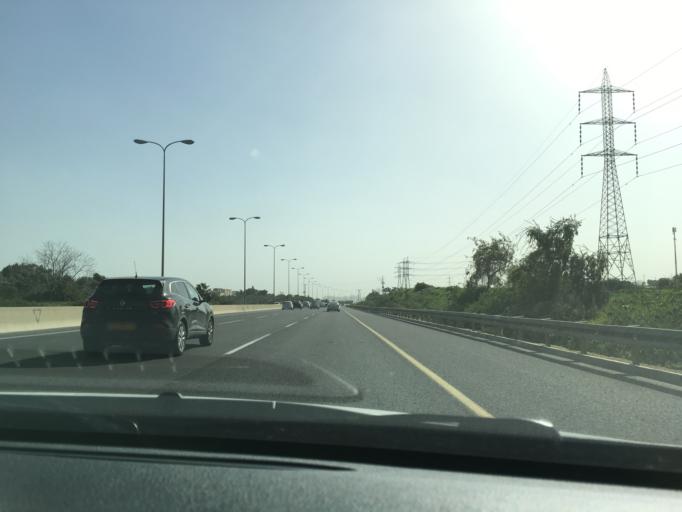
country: IL
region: Central District
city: Hod HaSharon
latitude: 32.1502
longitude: 34.8730
